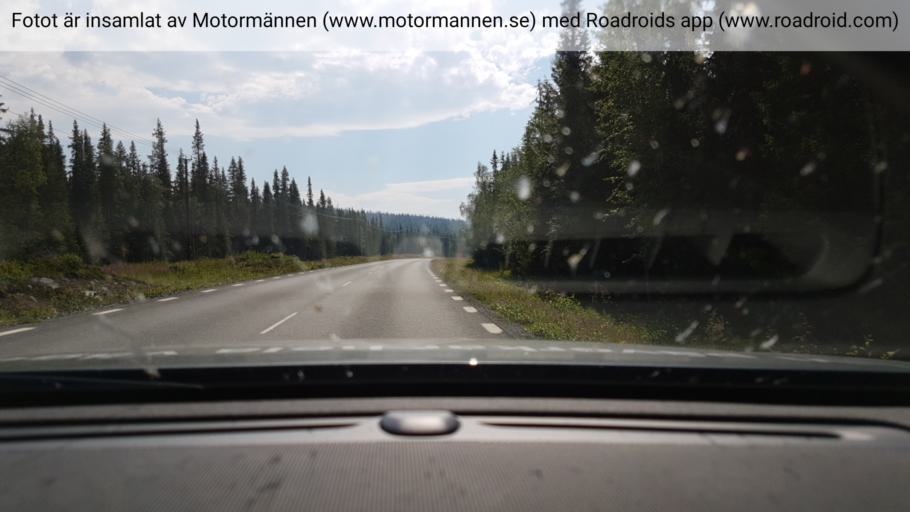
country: SE
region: Vaesterbotten
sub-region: Vilhelmina Kommun
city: Sjoberg
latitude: 65.5703
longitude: 15.5364
